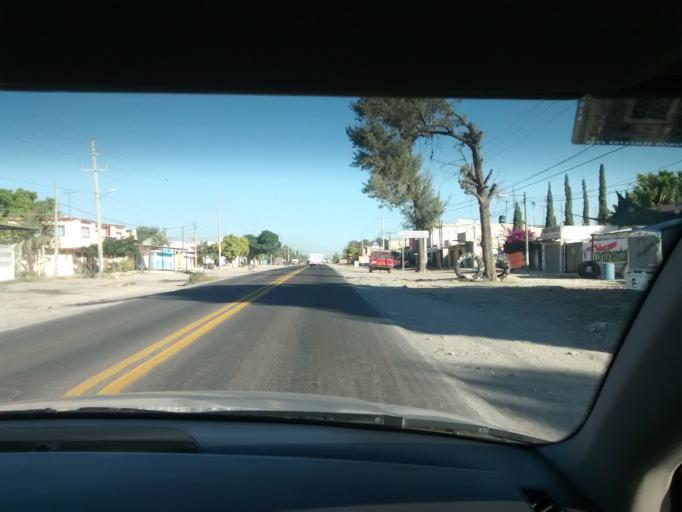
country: MX
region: Puebla
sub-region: Santiago Miahuatlan
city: San Jose Monte Chiquito
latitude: 18.4900
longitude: -97.4608
